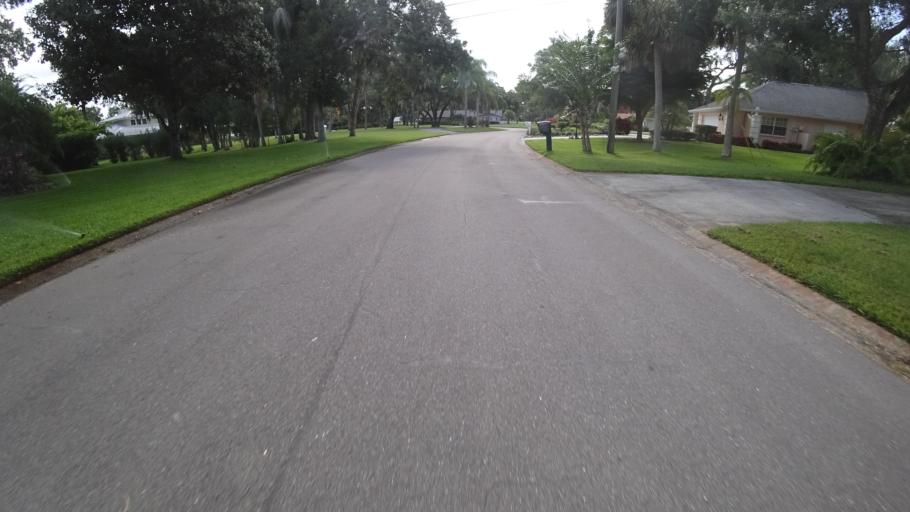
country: US
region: Florida
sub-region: Sarasota County
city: Desoto Lakes
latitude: 27.4014
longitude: -82.4922
